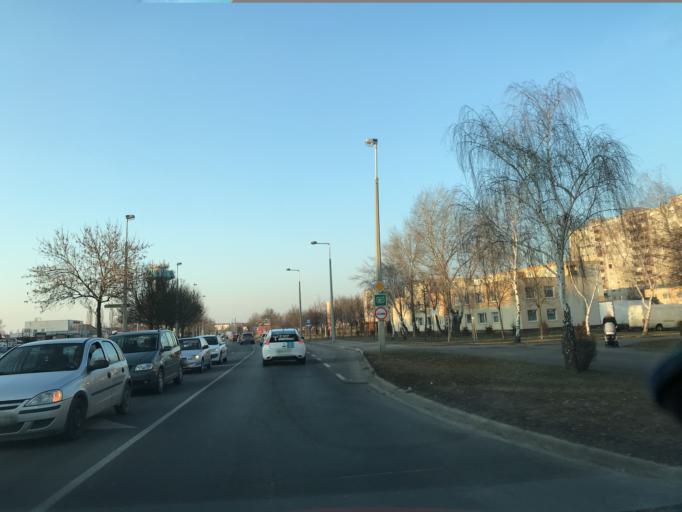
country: HU
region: Gyor-Moson-Sopron
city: Gyor
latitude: 47.6669
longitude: 17.6358
